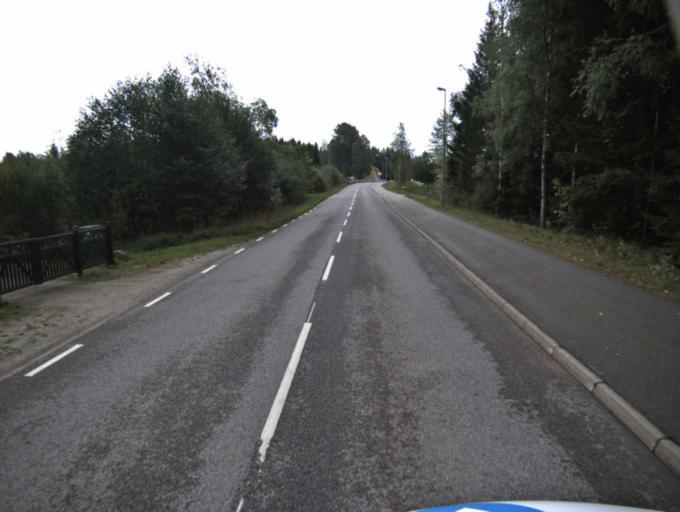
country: SE
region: Vaestra Goetaland
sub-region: Ulricehamns Kommun
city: Ulricehamn
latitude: 57.7756
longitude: 13.4309
